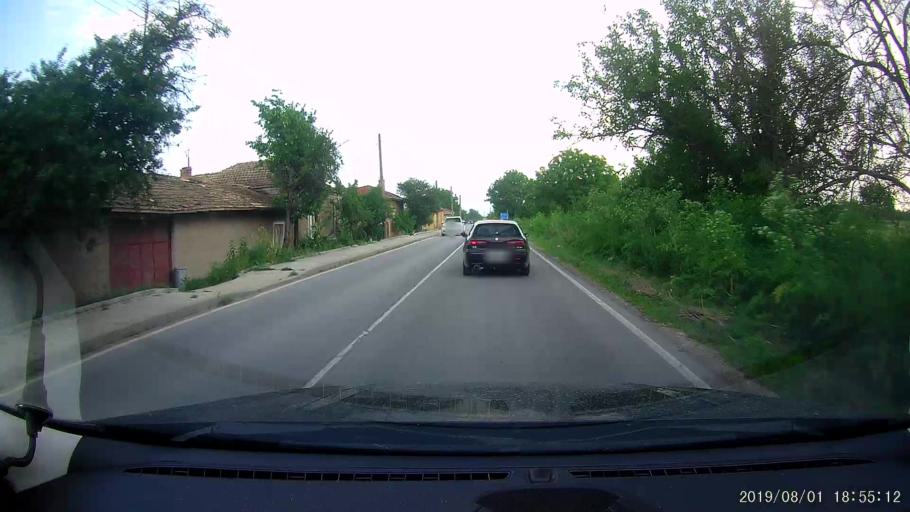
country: BG
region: Shumen
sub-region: Obshtina Smyadovo
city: Smyadovo
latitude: 43.1842
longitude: 27.0046
